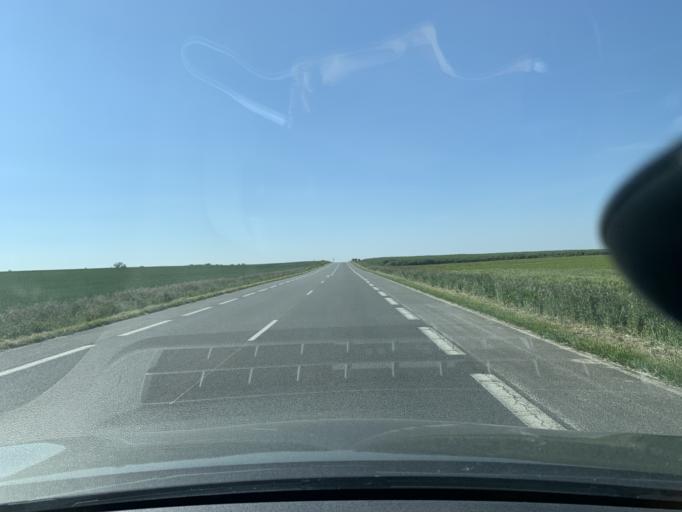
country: FR
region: Nord-Pas-de-Calais
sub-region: Departement du Nord
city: Cambrai
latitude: 50.1459
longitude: 3.2436
